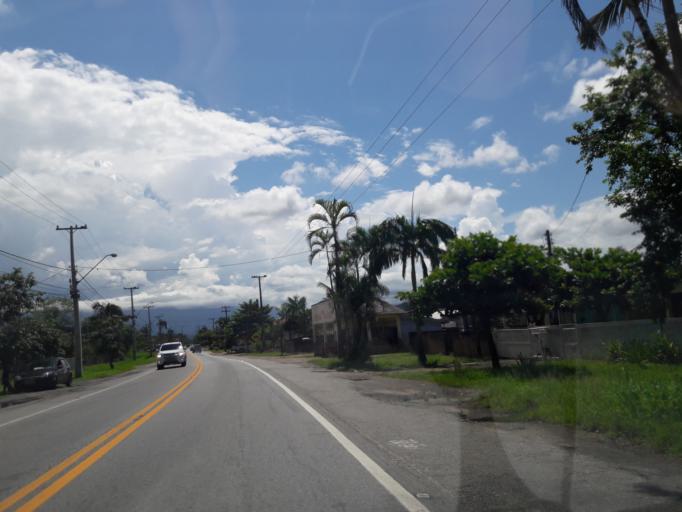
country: BR
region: Parana
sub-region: Antonina
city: Antonina
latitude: -25.4959
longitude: -48.8198
